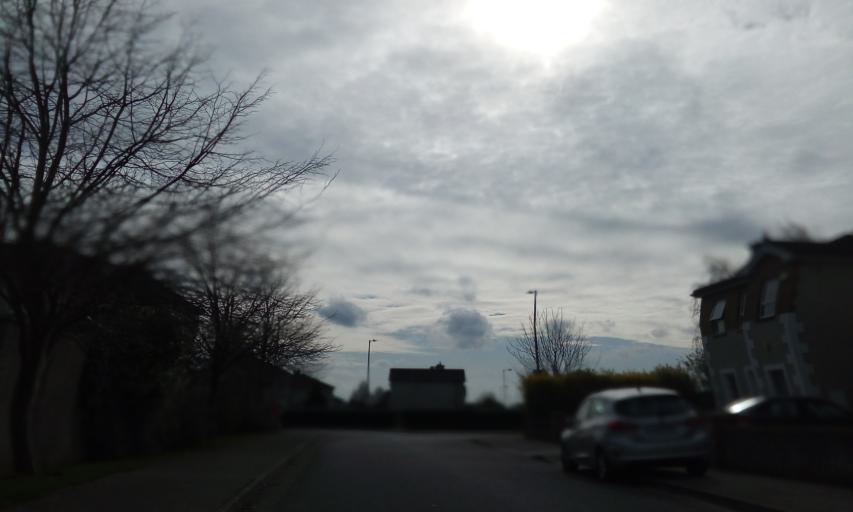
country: IE
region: Leinster
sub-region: Kilkenny
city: Kilkenny
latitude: 52.6663
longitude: -7.2330
